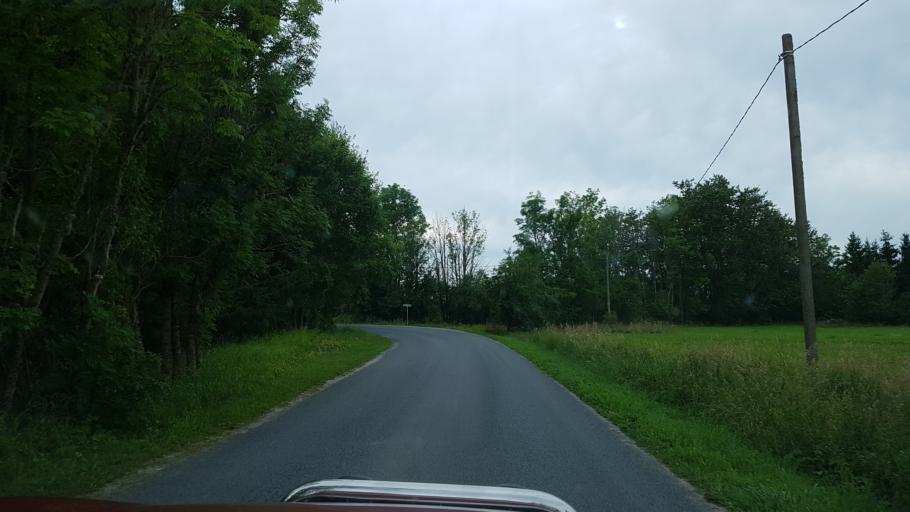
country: EE
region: Laeaene
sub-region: Ridala Parish
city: Uuemoisa
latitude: 58.8124
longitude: 23.6792
